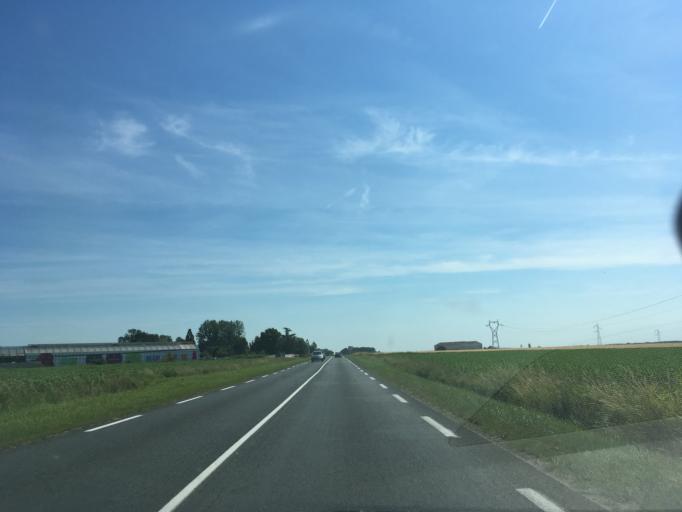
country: FR
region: Ile-de-France
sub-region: Departement de Seine-et-Marne
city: Bailly-Romainvilliers
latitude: 48.8515
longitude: 2.8410
